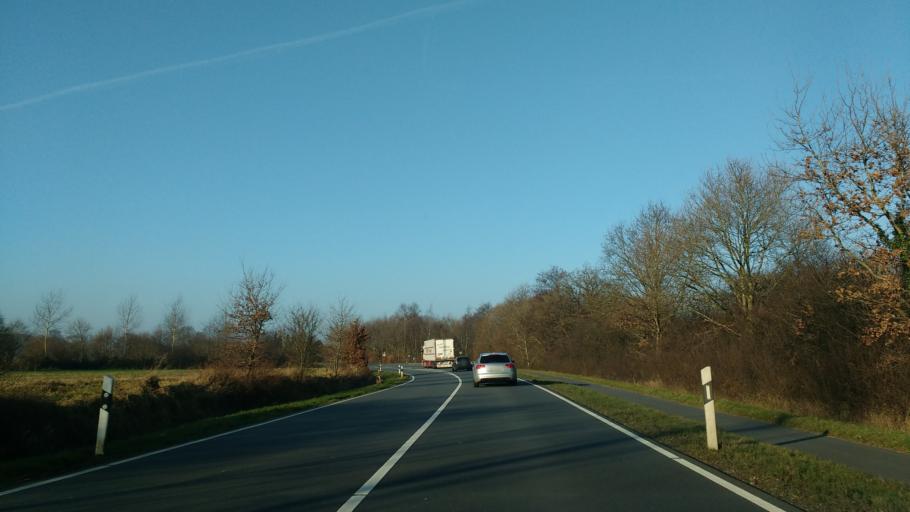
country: DE
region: Schleswig-Holstein
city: Hadenfeld
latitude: 54.0311
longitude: 9.4555
